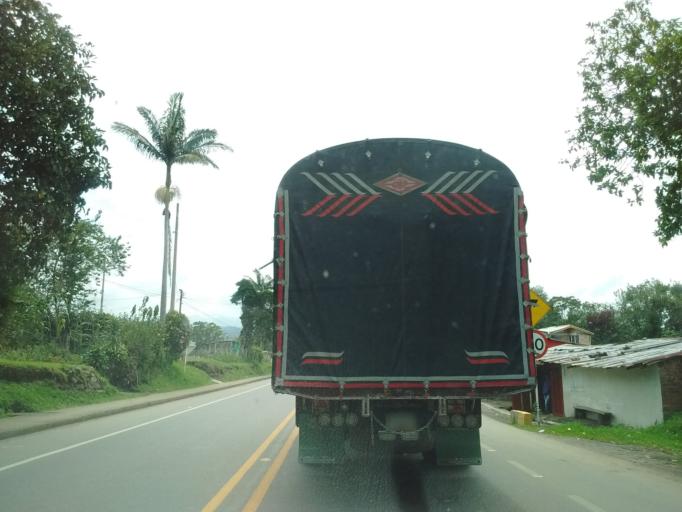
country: CO
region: Cauca
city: Cajibio
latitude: 2.5231
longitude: -76.5492
